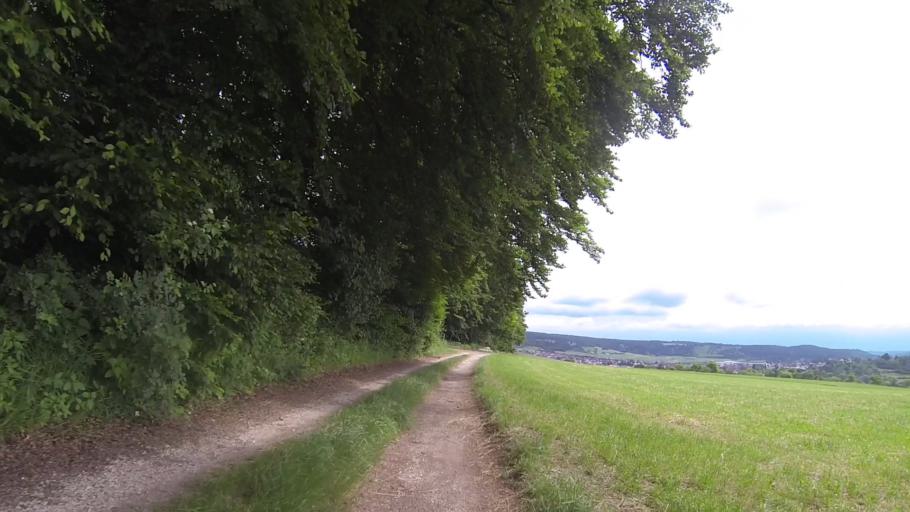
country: DE
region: Baden-Wuerttemberg
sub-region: Regierungsbezirk Stuttgart
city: Steinheim am Albuch
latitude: 48.6880
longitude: 10.0462
